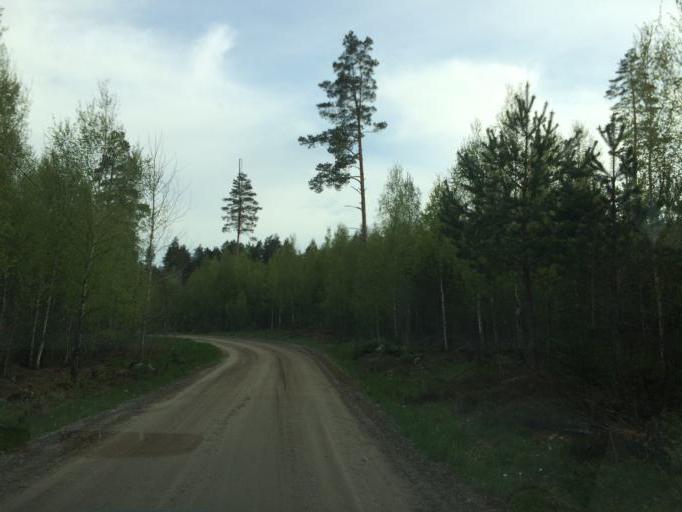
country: SE
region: Vaestmanland
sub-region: Kopings Kommun
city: Koping
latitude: 59.6131
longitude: 16.0472
